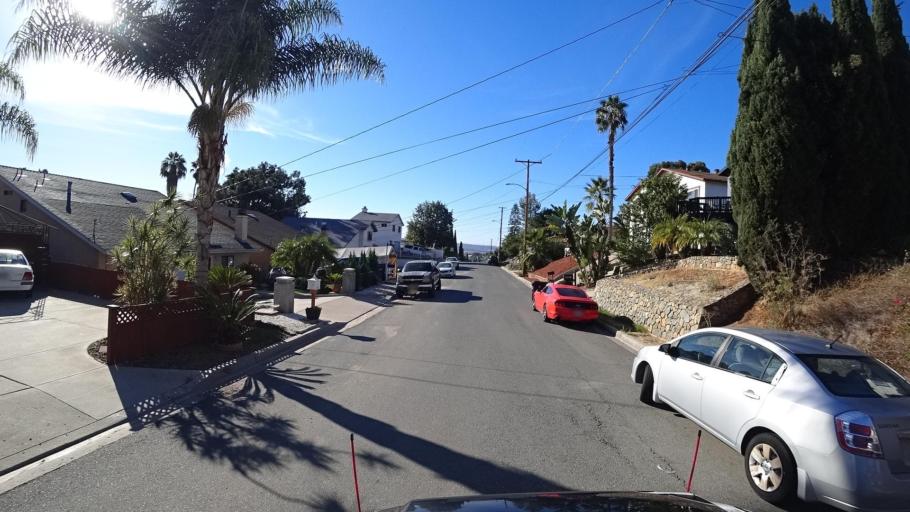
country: US
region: California
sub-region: San Diego County
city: La Presa
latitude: 32.7175
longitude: -116.9923
